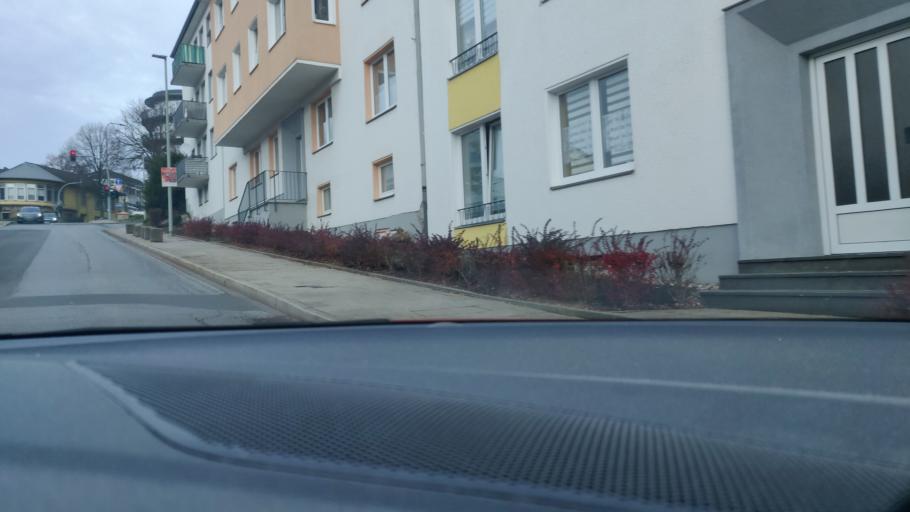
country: DE
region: North Rhine-Westphalia
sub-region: Regierungsbezirk Dusseldorf
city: Heiligenhaus
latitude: 51.3256
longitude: 6.9760
